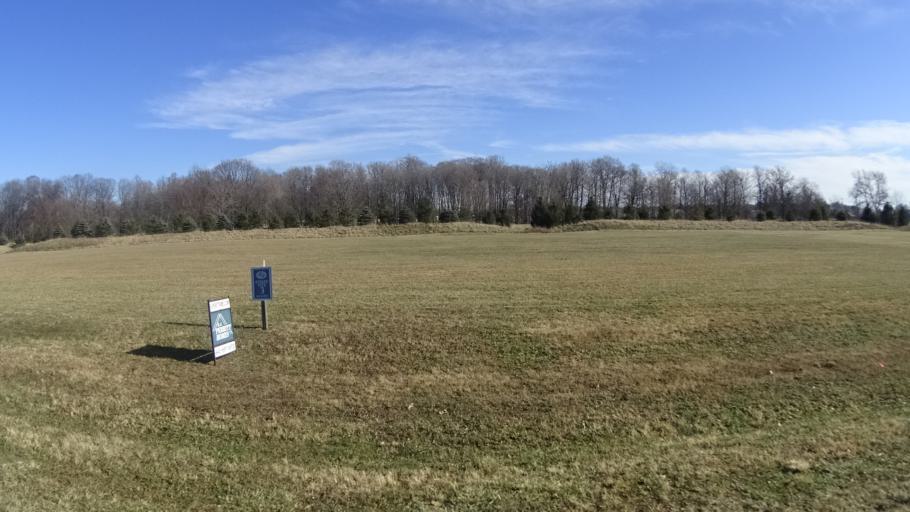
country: US
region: Ohio
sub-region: Lorain County
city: Vermilion-on-the-Lake
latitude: 41.3550
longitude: -82.3277
